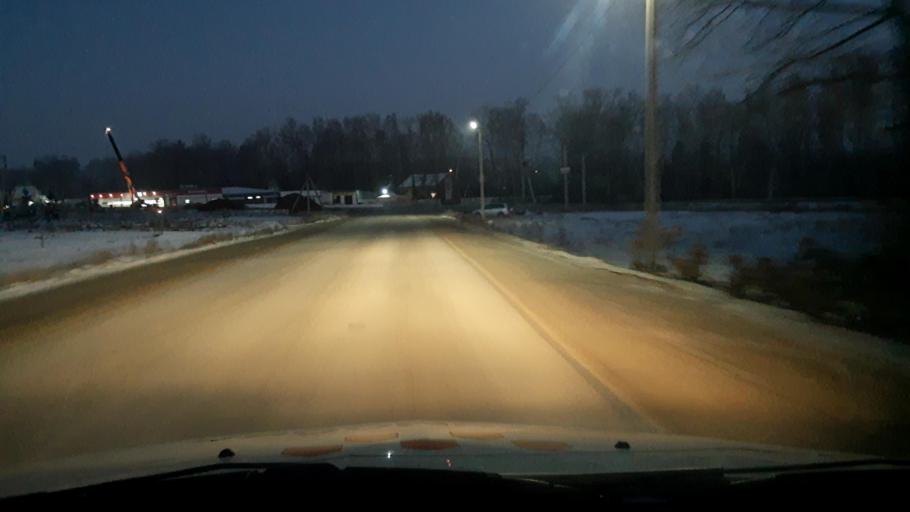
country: RU
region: Bashkortostan
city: Iglino
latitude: 54.8300
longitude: 56.4304
